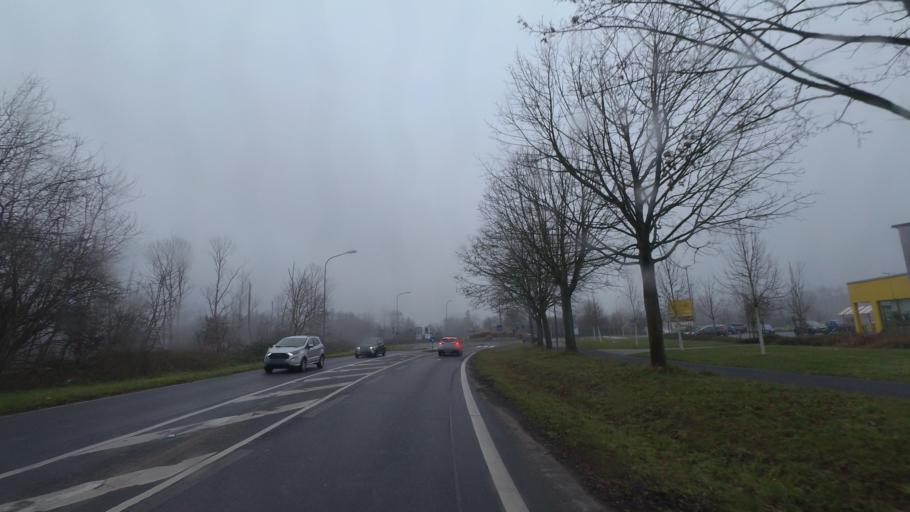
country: DE
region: Hesse
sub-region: Regierungsbezirk Darmstadt
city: Seligenstadt
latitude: 50.0525
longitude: 8.9453
